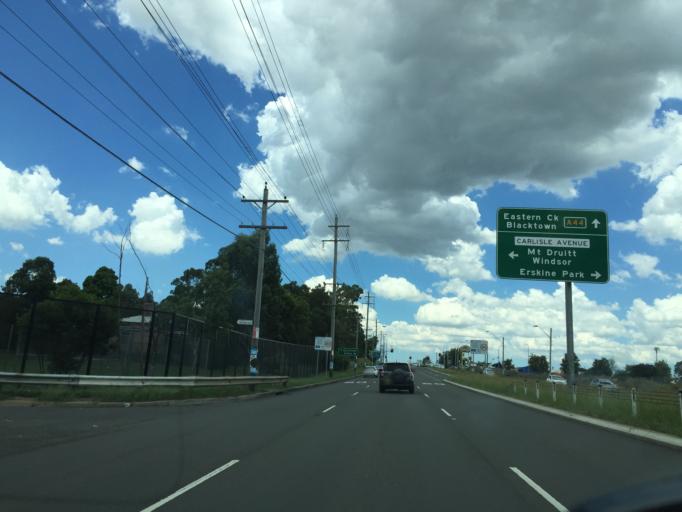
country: AU
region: New South Wales
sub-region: Blacktown
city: Mount Druitt
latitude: -33.7785
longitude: 150.8119
